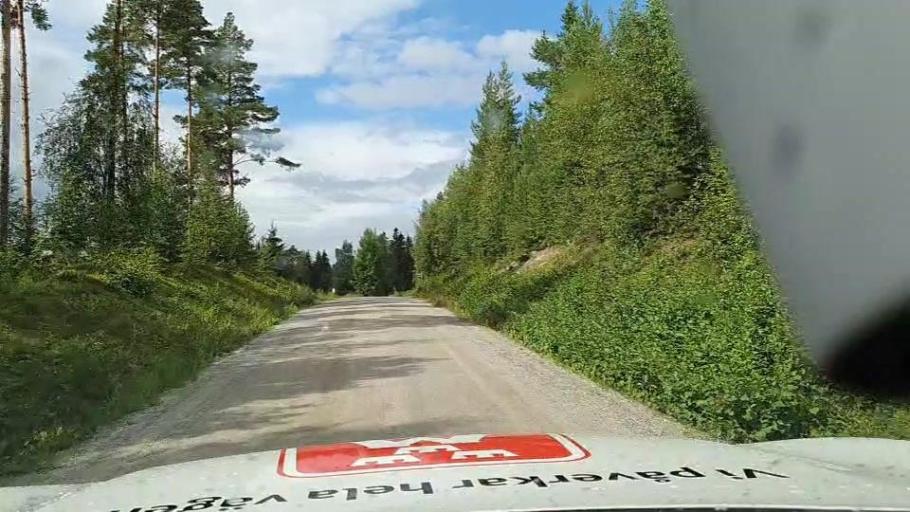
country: SE
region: Jaemtland
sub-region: Braecke Kommun
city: Braecke
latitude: 63.1018
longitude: 15.7535
